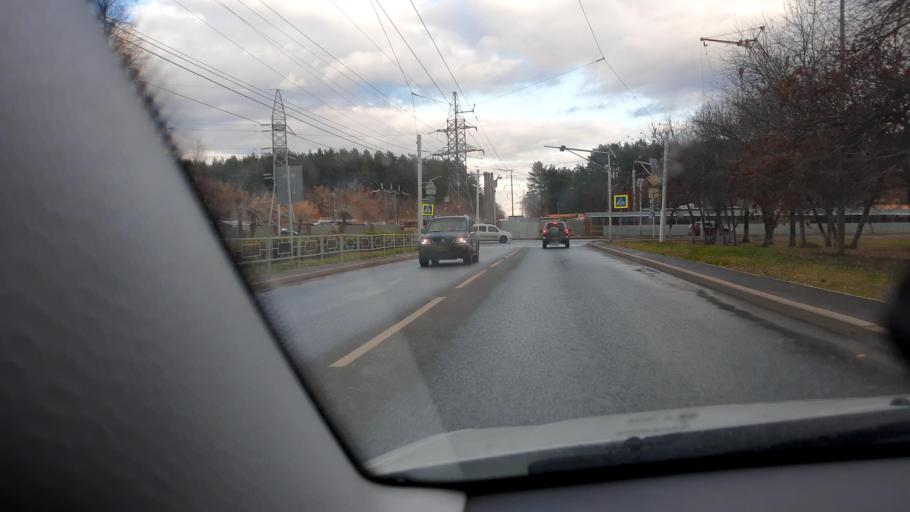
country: RU
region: Bashkortostan
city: Ufa
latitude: 54.7021
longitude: 56.0056
